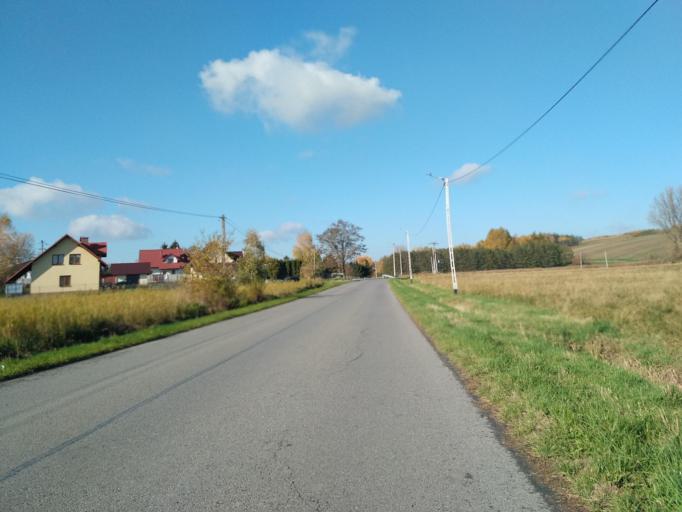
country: PL
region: Subcarpathian Voivodeship
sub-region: Powiat rzeszowski
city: Zglobien
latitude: 50.0321
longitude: 21.8558
